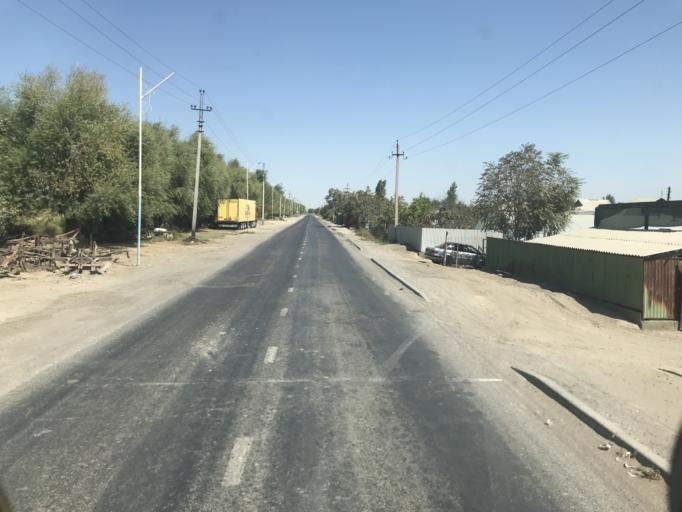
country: KZ
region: Ongtustik Qazaqstan
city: Ilyich
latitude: 40.9381
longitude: 68.4883
